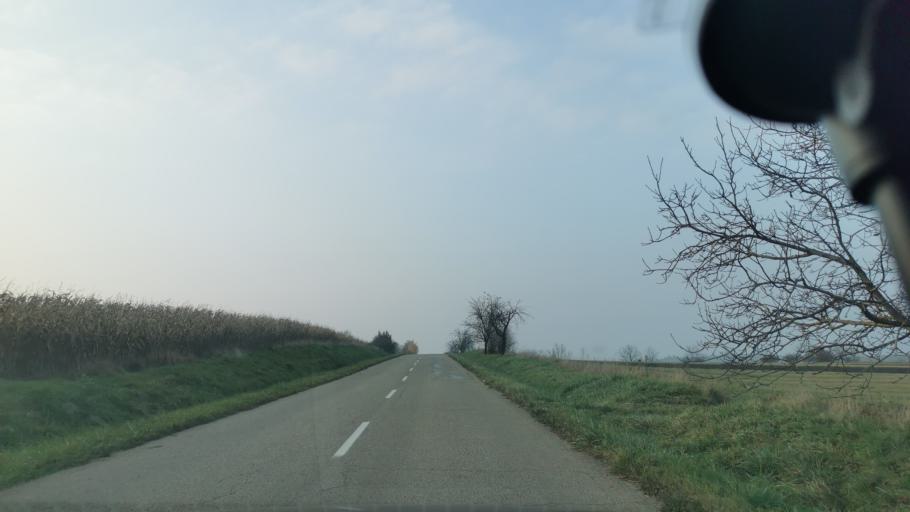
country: SK
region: Trnavsky
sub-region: Okres Skalica
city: Holic
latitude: 48.8016
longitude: 17.1850
